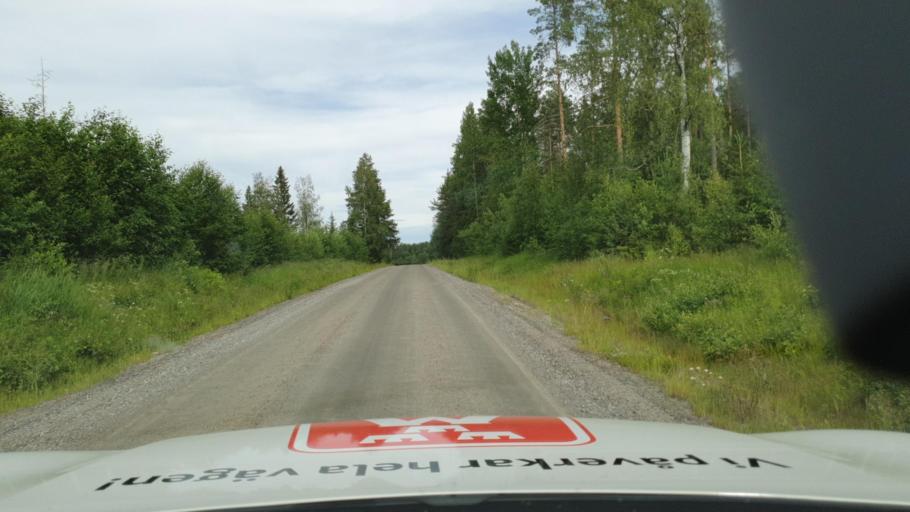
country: SE
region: Vaesterbotten
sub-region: Skelleftea Kommun
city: Viken
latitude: 64.5097
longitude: 20.9339
